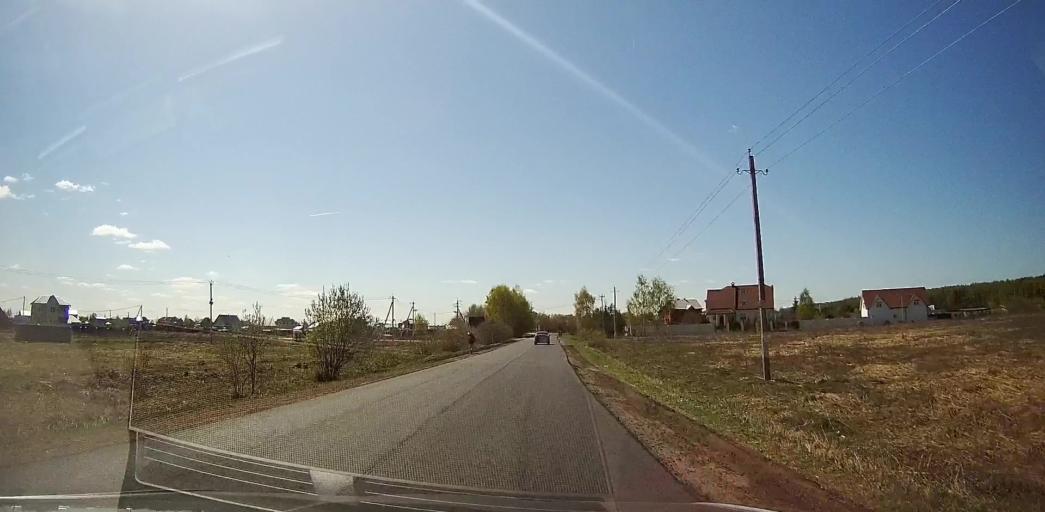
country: RU
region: Moskovskaya
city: Malyshevo
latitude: 55.4708
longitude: 38.3922
